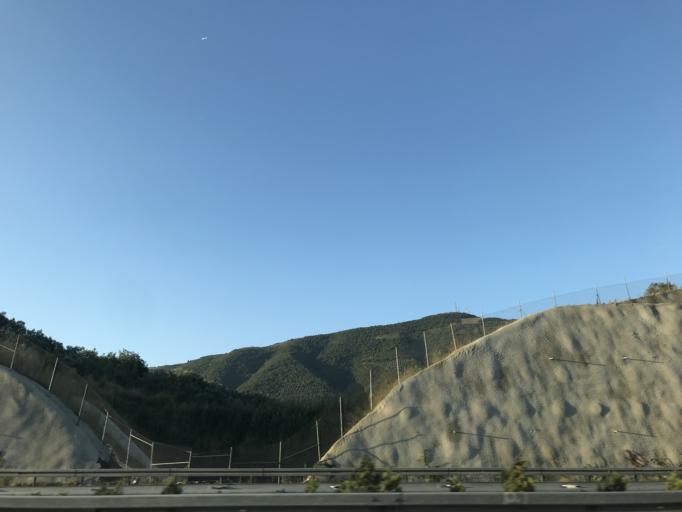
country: TR
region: Bursa
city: Umurbey
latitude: 40.4271
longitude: 29.2146
